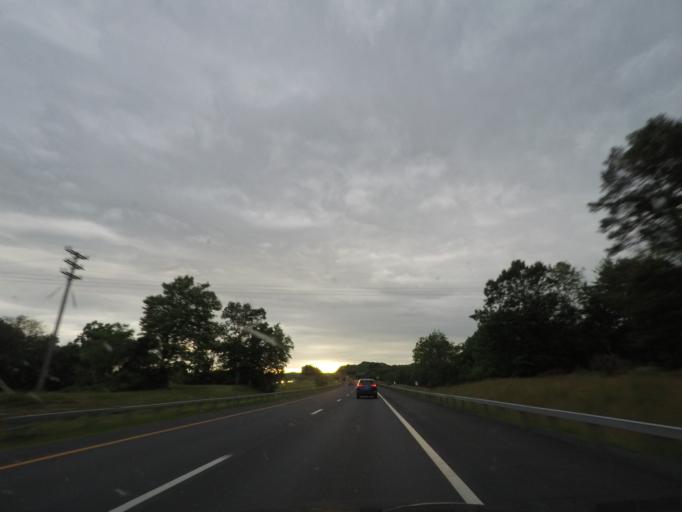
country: US
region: New York
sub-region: Rensselaer County
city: Nassau
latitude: 42.4821
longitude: -73.6288
